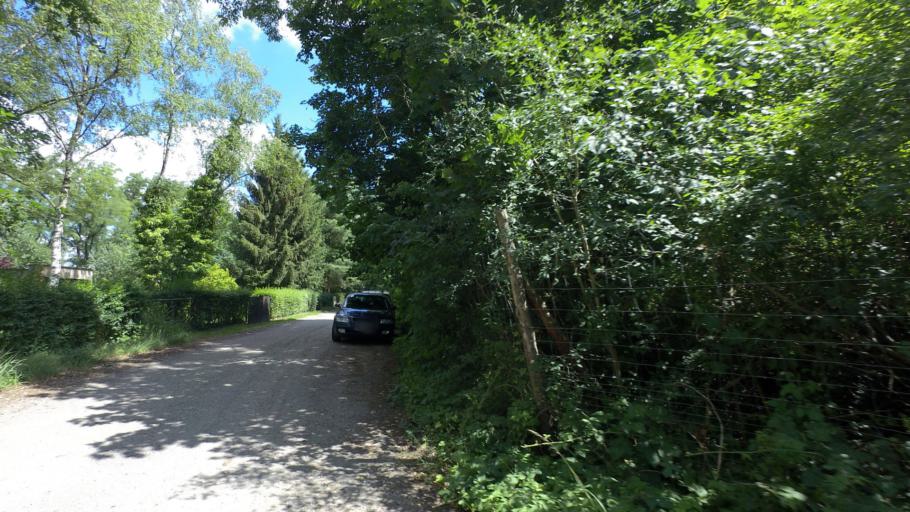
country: DE
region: Brandenburg
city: Finsterwalde
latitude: 51.6463
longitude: 13.6879
